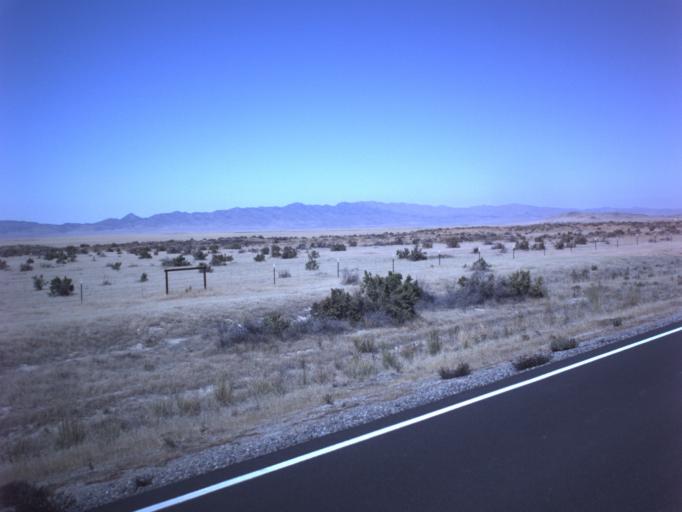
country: US
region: Utah
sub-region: Tooele County
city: Grantsville
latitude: 40.3214
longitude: -112.7438
